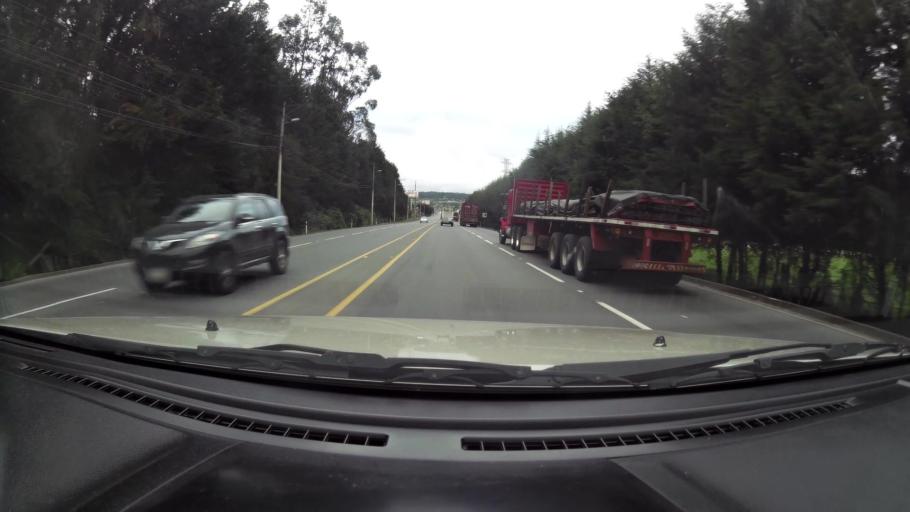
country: EC
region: Pichincha
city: Machachi
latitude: -0.4460
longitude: -78.6009
